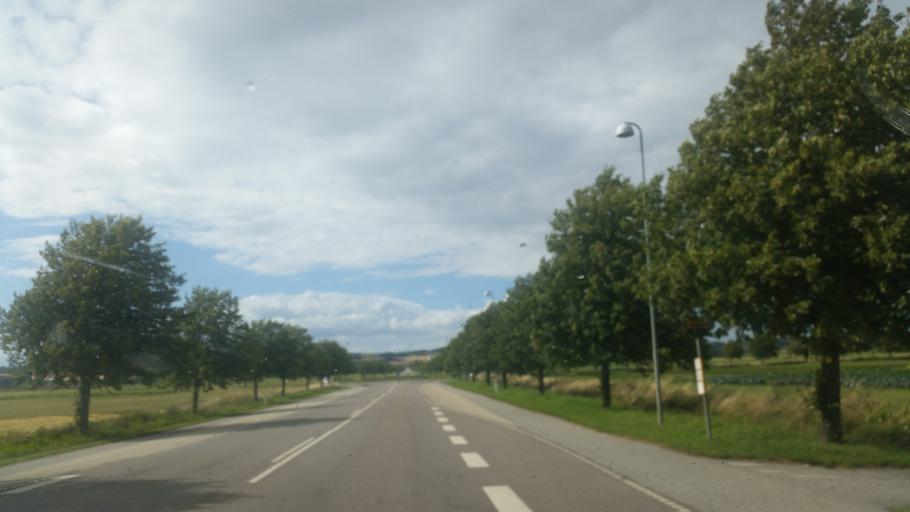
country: DK
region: Zealand
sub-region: Odsherred Kommune
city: Horve
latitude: 55.7910
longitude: 11.4596
